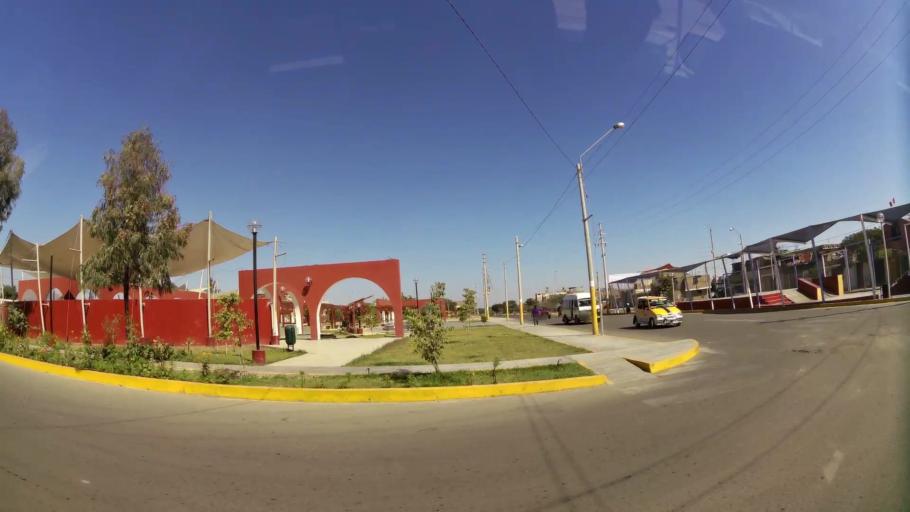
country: PE
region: Ica
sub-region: Provincia de Ica
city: La Tinguina
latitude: -14.0317
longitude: -75.7073
